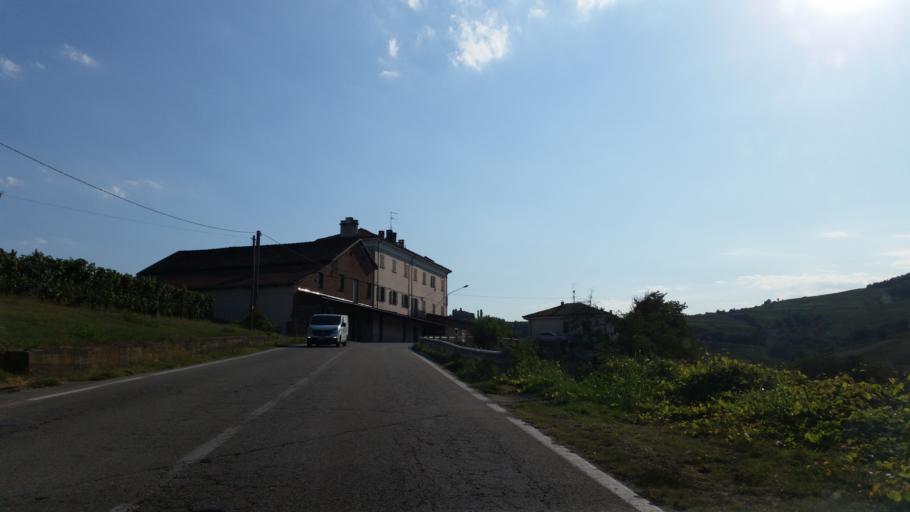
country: IT
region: Piedmont
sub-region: Provincia di Cuneo
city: Barolo
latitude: 44.6240
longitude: 7.9530
